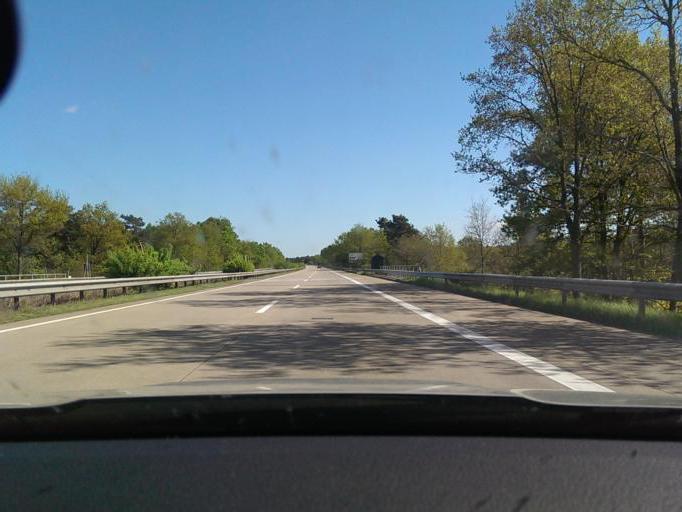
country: DE
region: Lower Saxony
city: Verden
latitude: 52.9494
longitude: 9.2552
